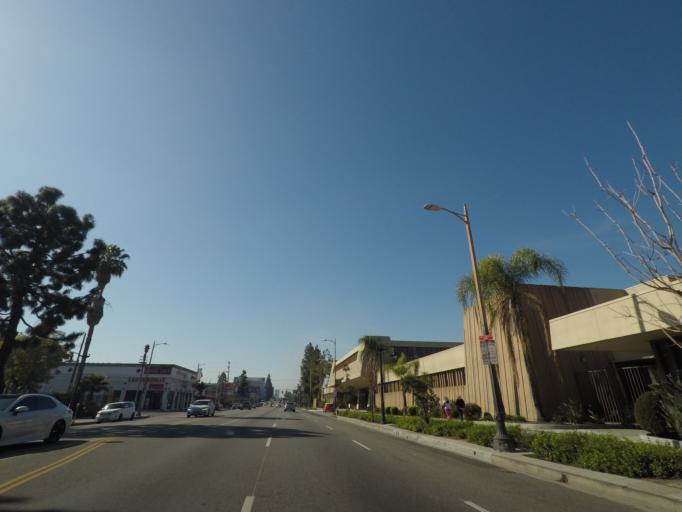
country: US
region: California
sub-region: Los Angeles County
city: Silver Lake
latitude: 34.0852
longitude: -118.2918
